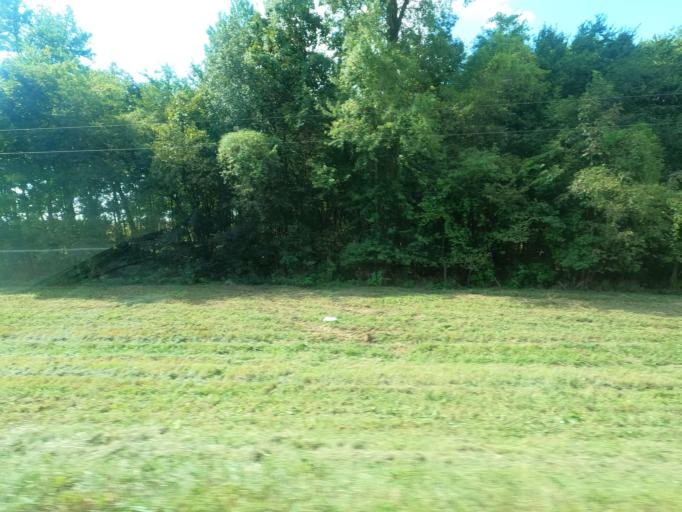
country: US
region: Illinois
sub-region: Massac County
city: Metropolis
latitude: 37.2835
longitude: -88.7579
